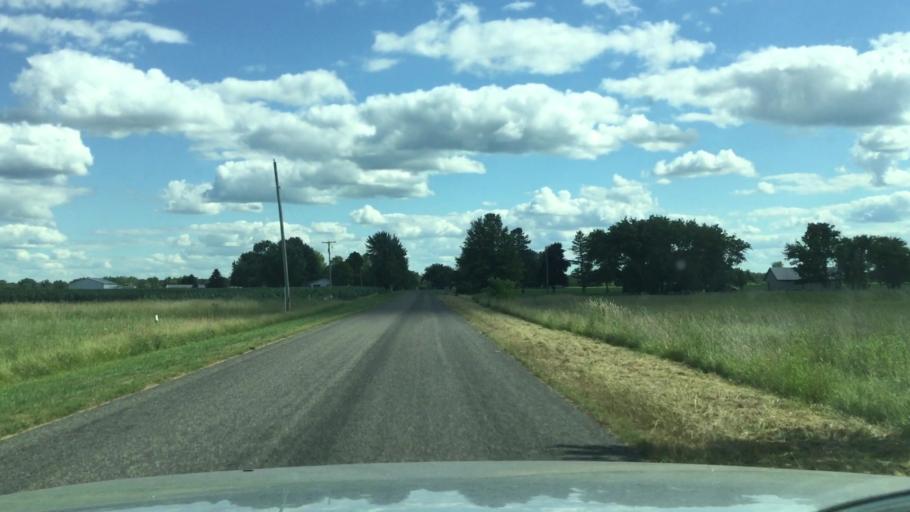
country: US
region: Michigan
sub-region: Saginaw County
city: Hemlock
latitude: 43.3772
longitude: -84.1606
